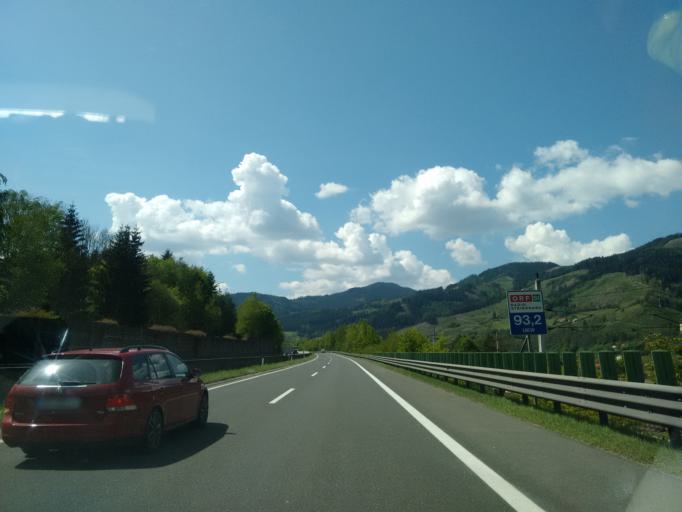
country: AT
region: Styria
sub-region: Politischer Bezirk Bruck-Muerzzuschlag
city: Oberaich
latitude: 47.4062
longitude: 15.2135
